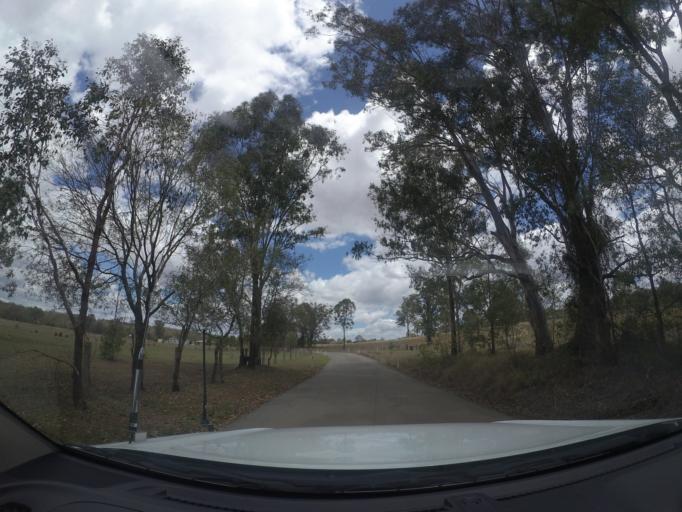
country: AU
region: Queensland
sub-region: Logan
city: Cedar Vale
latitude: -27.9399
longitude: 153.0661
